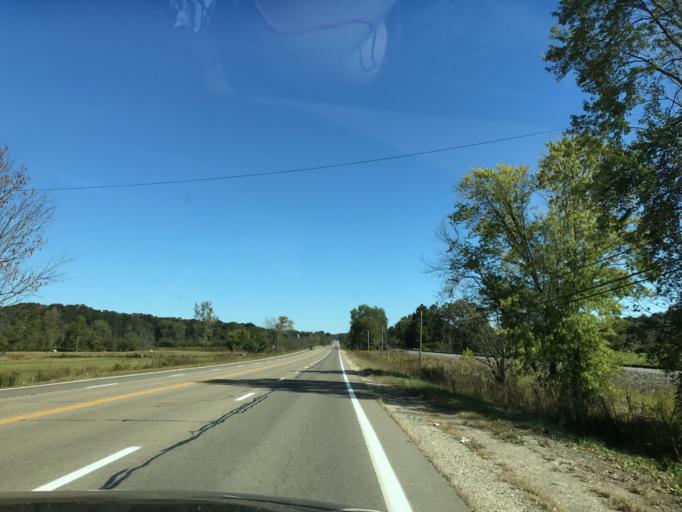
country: US
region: Ohio
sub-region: Guernsey County
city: Cambridge
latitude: 40.0108
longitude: -81.6519
